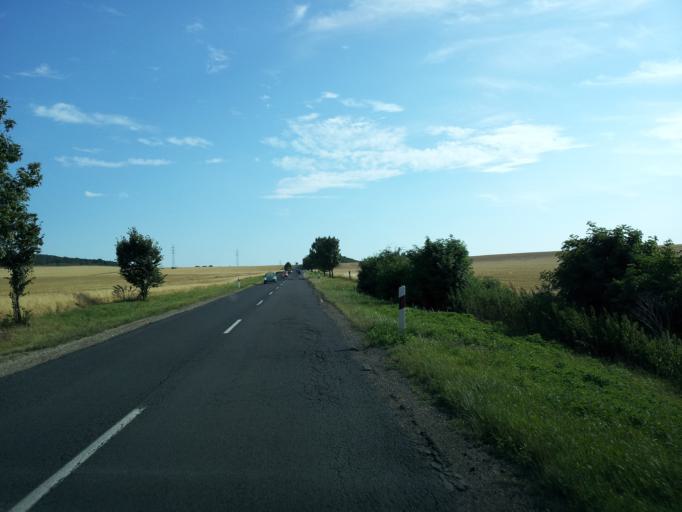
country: HU
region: Veszprem
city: Nemesvamos
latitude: 47.0379
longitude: 17.8194
